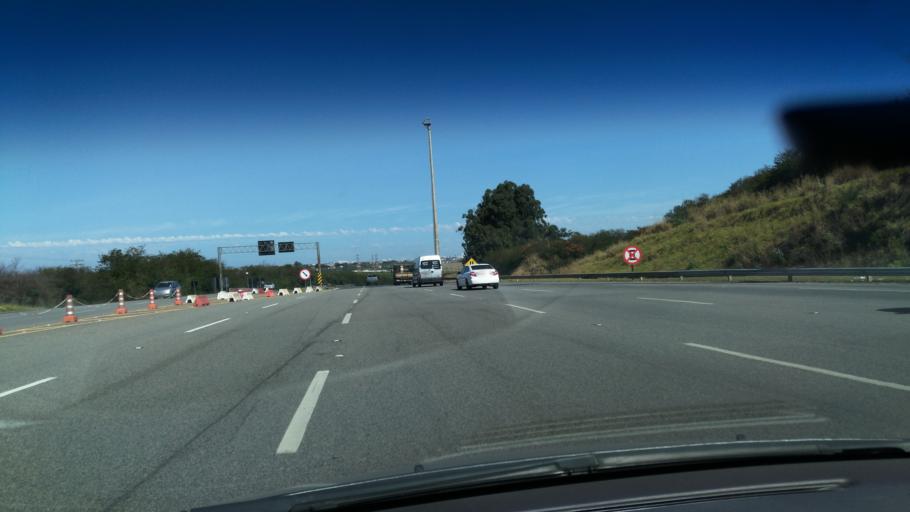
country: BR
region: Sao Paulo
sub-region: Jaguariuna
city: Jaguariuna
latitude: -22.7731
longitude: -47.0224
